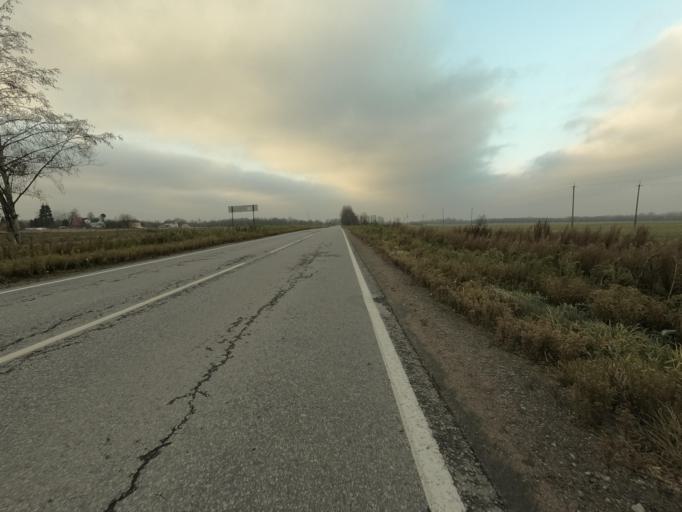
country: RU
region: Leningrad
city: Mga
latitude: 59.7647
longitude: 31.0176
